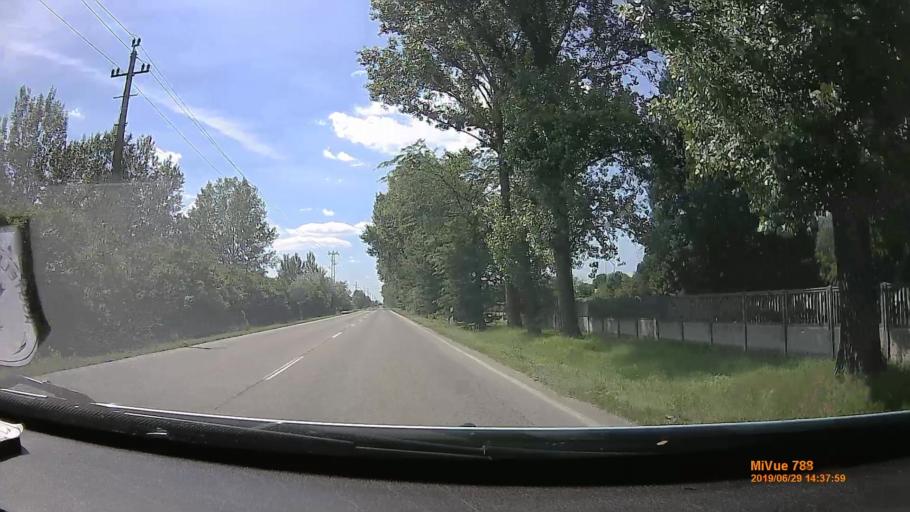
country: HU
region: Komarom-Esztergom
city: Tat
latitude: 47.7504
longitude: 18.6273
